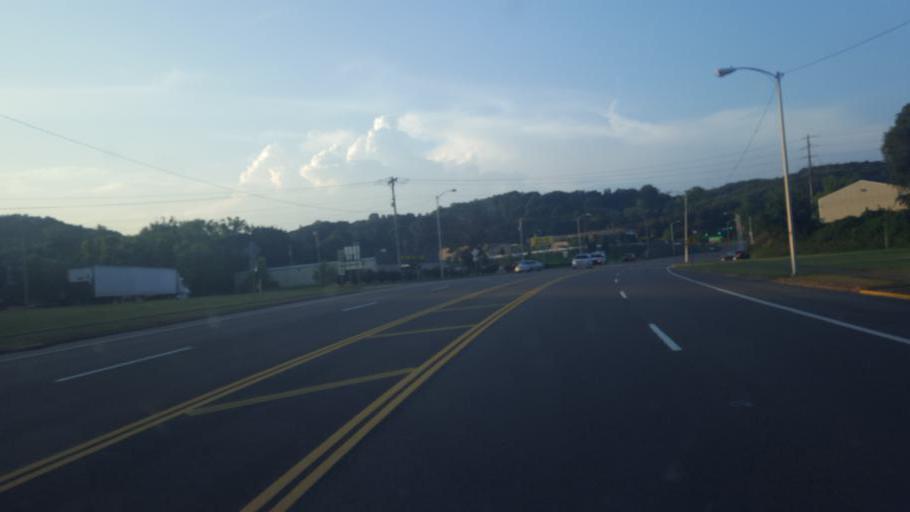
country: US
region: Tennessee
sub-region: Sullivan County
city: Kingsport
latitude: 36.5601
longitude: -82.5680
